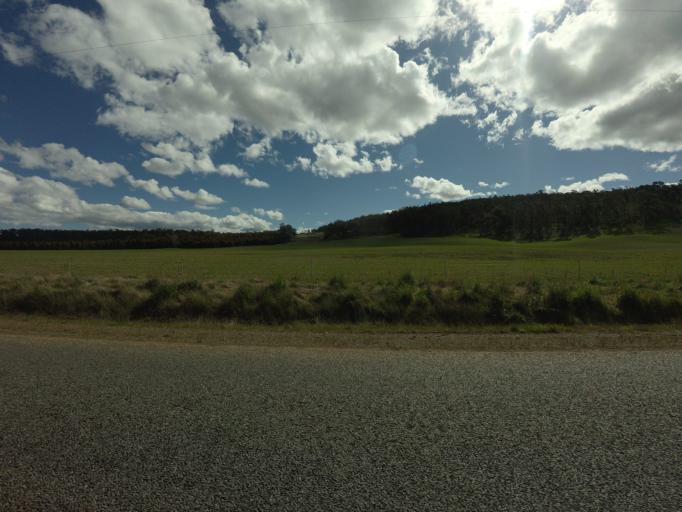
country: AU
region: Tasmania
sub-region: Brighton
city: Bridgewater
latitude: -42.4508
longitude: 147.3123
